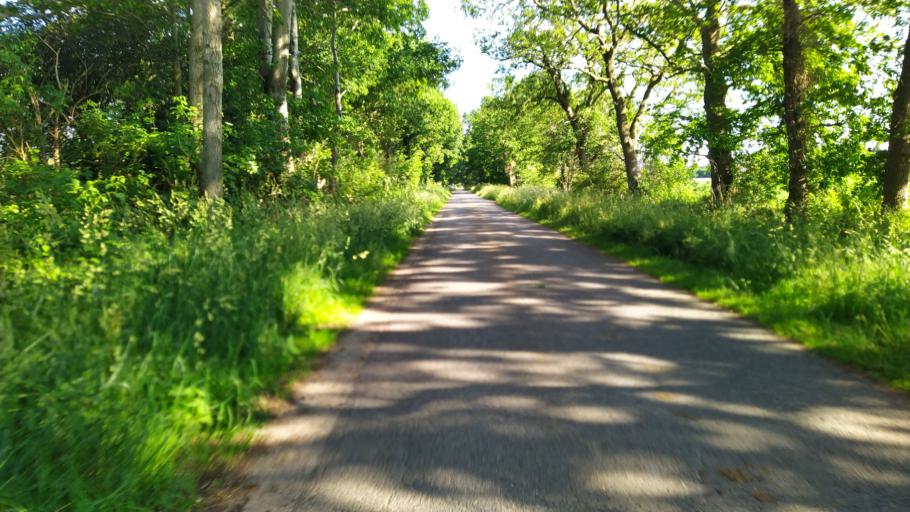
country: DE
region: Lower Saxony
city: Lintig
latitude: 53.6096
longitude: 8.8900
